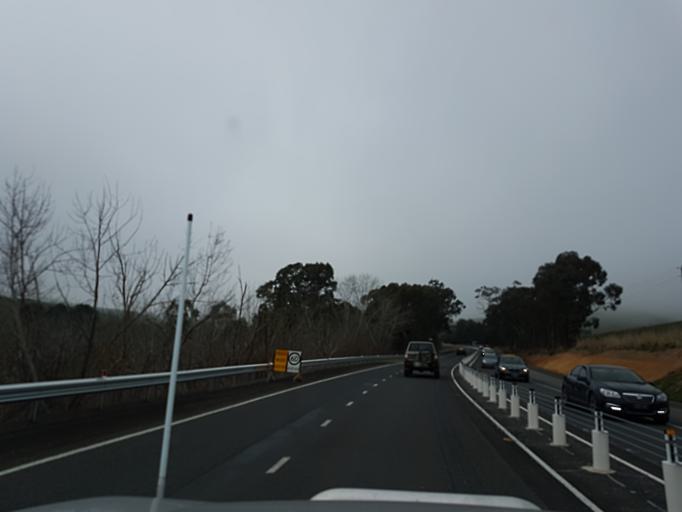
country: AU
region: Victoria
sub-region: Murrindindi
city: Alexandra
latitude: -37.1952
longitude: 145.4769
